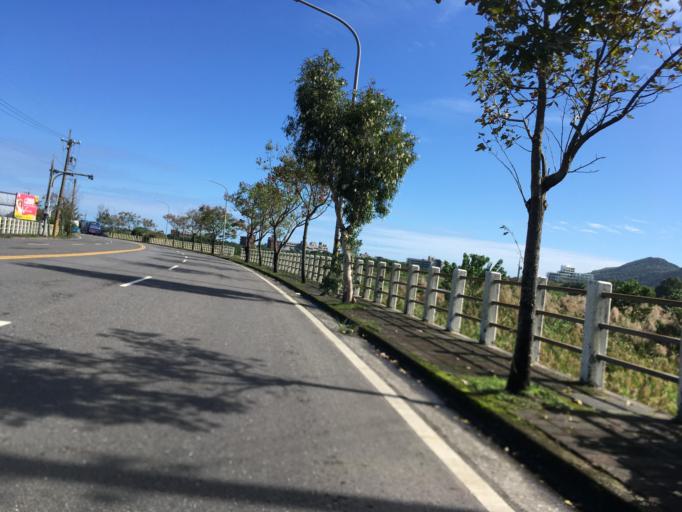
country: TW
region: Taiwan
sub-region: Yilan
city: Yilan
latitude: 24.6119
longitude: 121.8407
